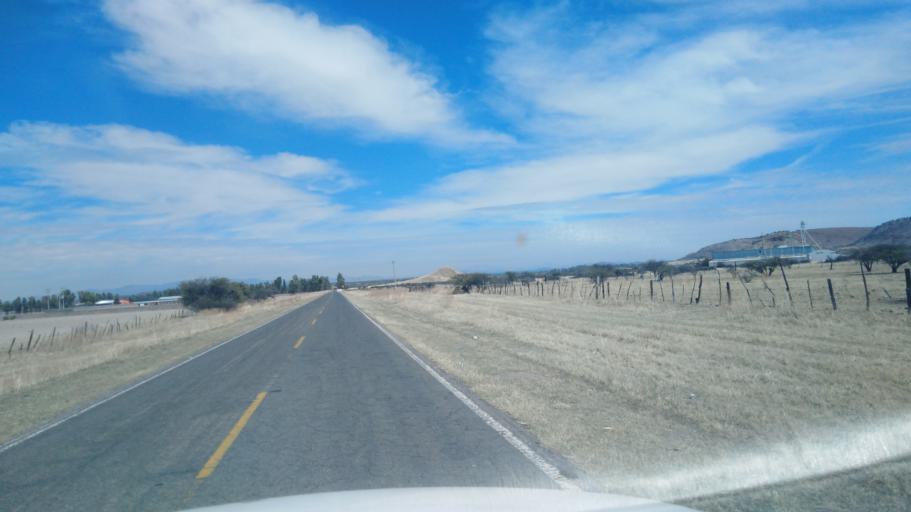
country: MX
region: Durango
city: Victoria de Durango
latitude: 24.1798
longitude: -104.6891
